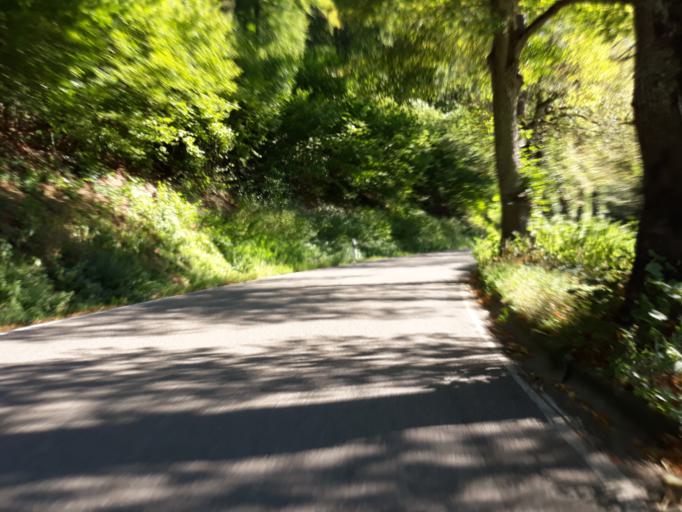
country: DE
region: Baden-Wuerttemberg
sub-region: Regierungsbezirk Stuttgart
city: Aidlingen
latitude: 48.6706
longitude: 8.9146
